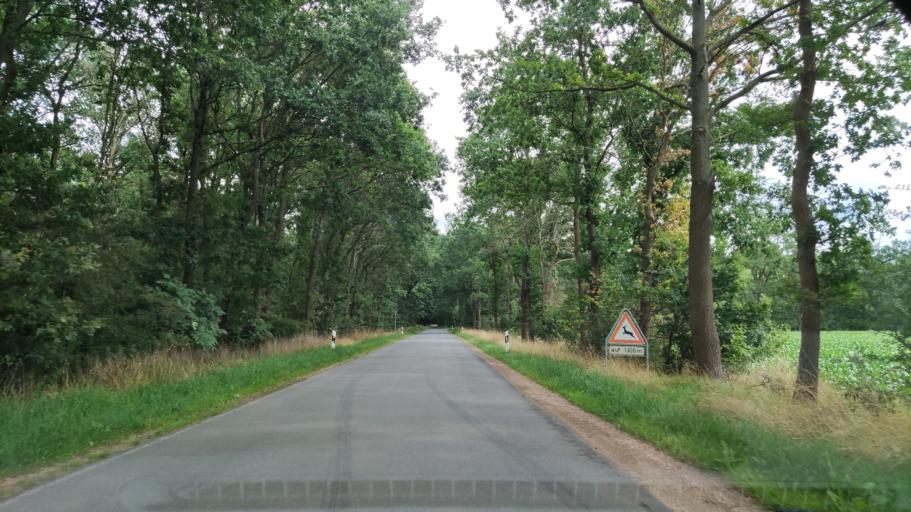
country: DE
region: Lower Saxony
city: Dannenberg
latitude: 53.0942
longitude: 11.1262
